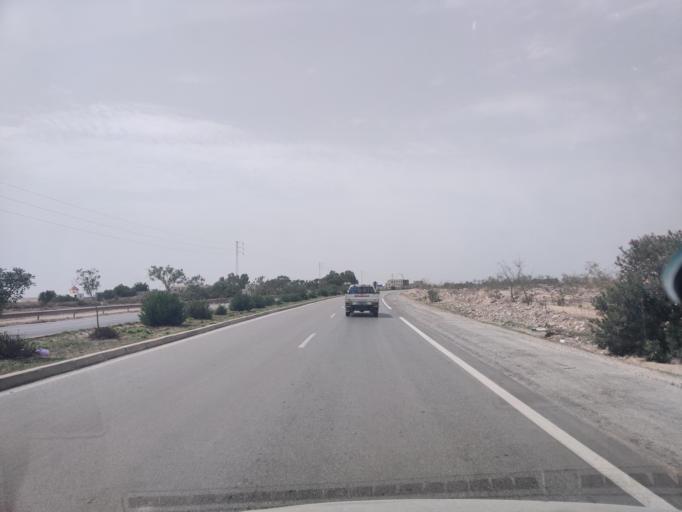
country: TN
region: Susah
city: Akouda
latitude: 35.8356
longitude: 10.5496
